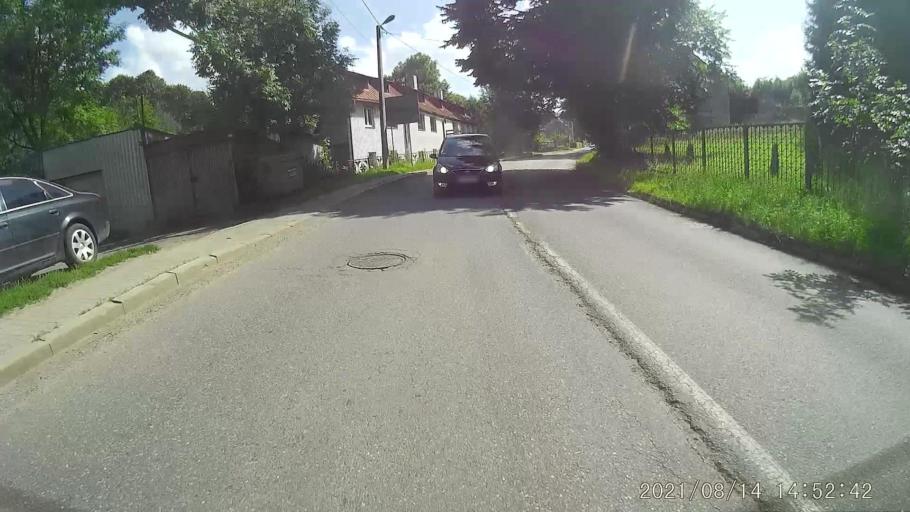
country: PL
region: Lower Silesian Voivodeship
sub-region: Powiat walbrzyski
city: Gluszyca Gorna
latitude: 50.6692
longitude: 16.3763
